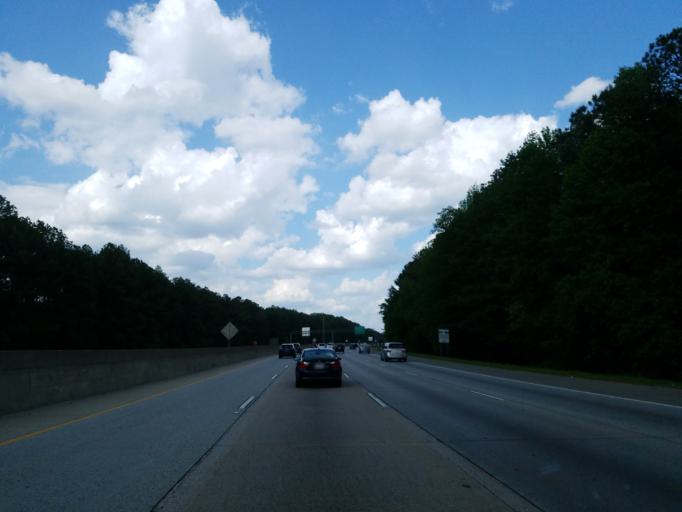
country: US
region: Georgia
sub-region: Fulton County
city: Alpharetta
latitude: 34.0497
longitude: -84.2996
